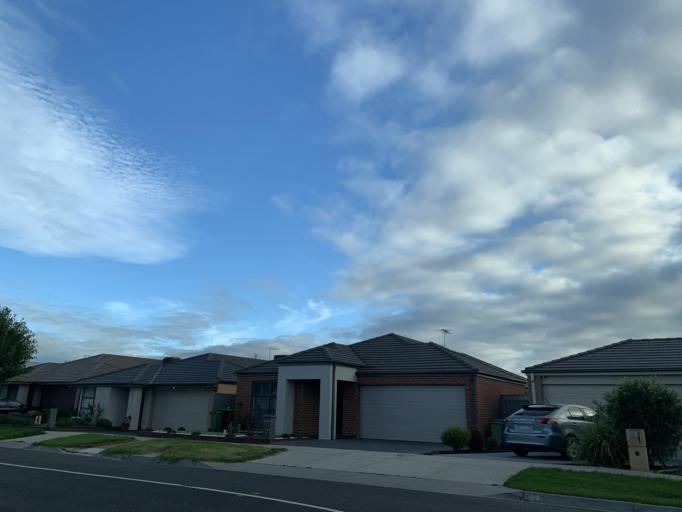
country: AU
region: Victoria
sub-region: Casey
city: Cranbourne East
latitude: -38.1258
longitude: 145.3064
